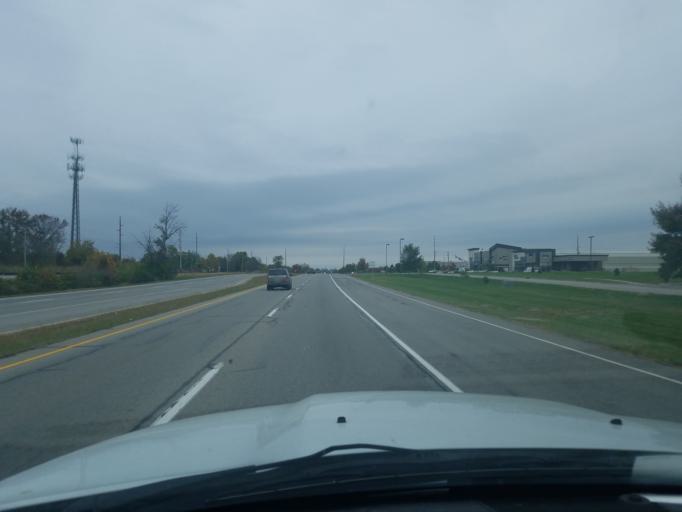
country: US
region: Indiana
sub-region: Clark County
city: Oak Park
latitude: 38.3671
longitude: -85.6978
